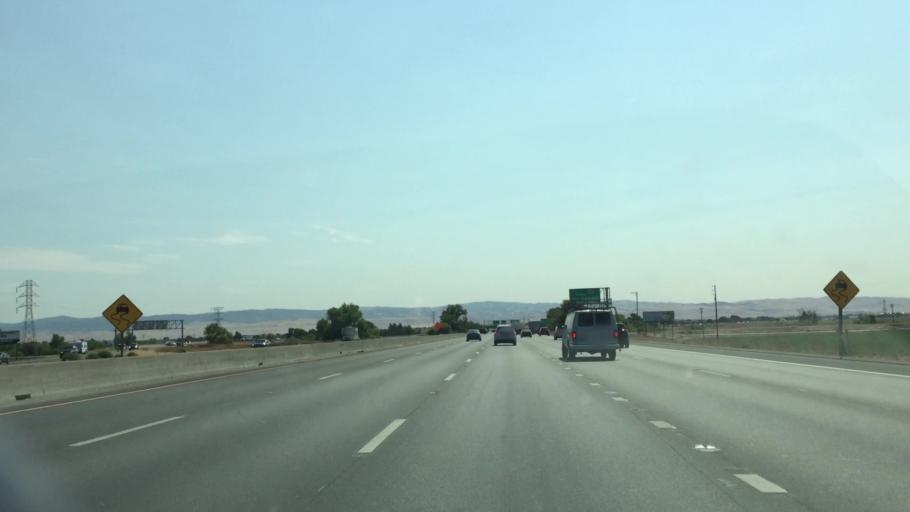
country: US
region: California
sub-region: San Joaquin County
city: Lathrop
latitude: 37.7715
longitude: -121.3205
